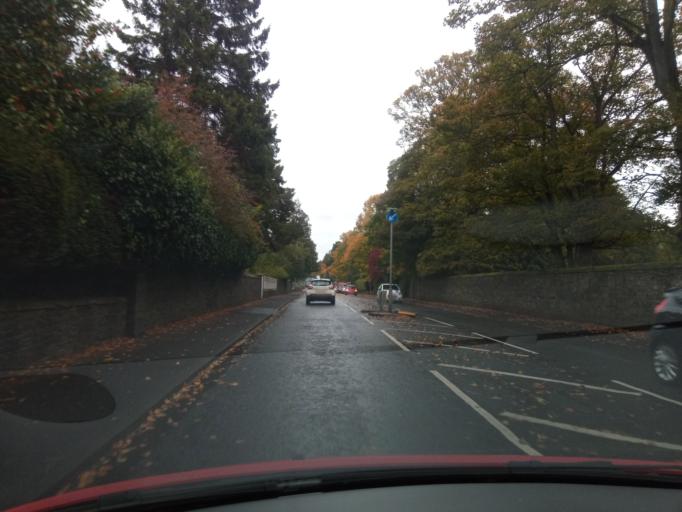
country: GB
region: Scotland
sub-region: The Scottish Borders
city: Galashiels
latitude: 55.6105
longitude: -2.8002
